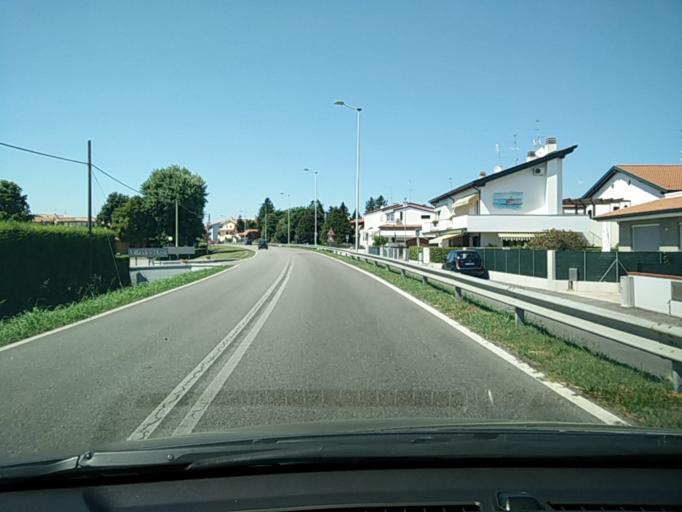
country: IT
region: Veneto
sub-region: Provincia di Venezia
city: La Salute di Livenza
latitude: 45.6460
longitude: 12.8429
